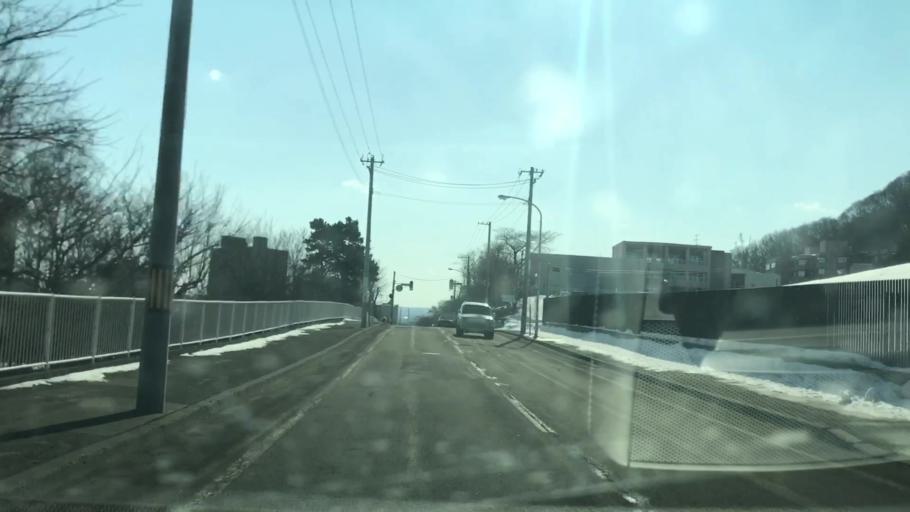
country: JP
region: Hokkaido
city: Sapporo
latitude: 43.0351
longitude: 141.3304
